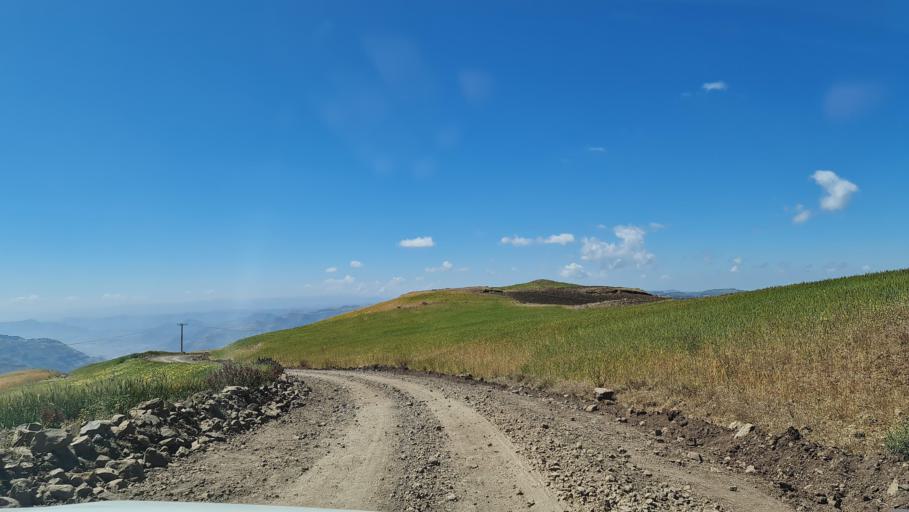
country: ET
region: Amhara
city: Debark'
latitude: 13.2326
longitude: 38.1028
